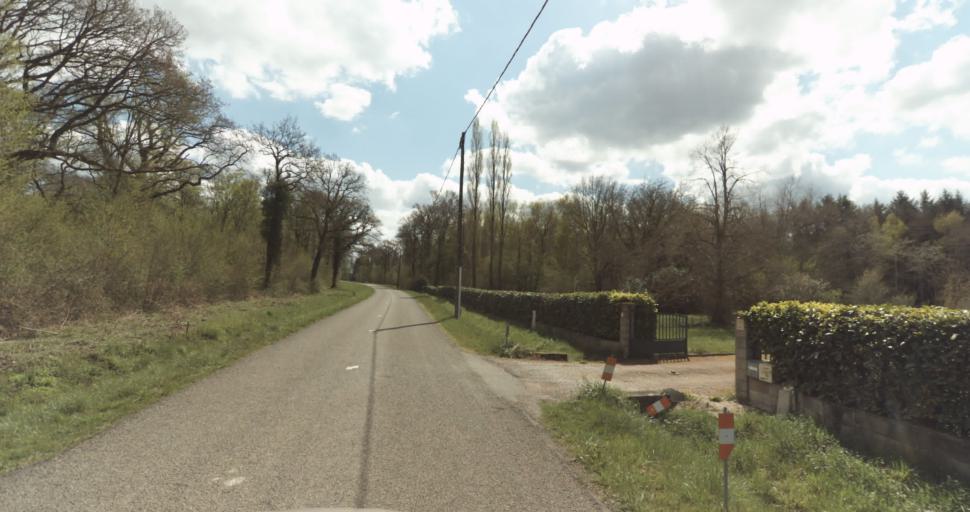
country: FR
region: Bourgogne
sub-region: Departement de la Cote-d'Or
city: Auxonne
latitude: 47.1744
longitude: 5.4245
